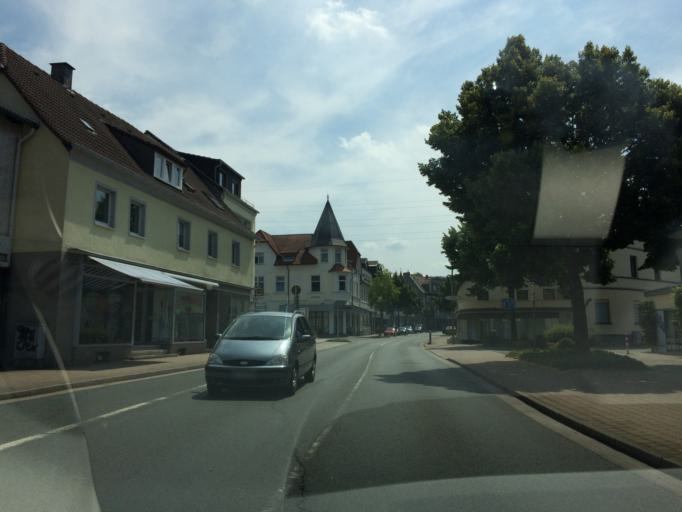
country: DE
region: North Rhine-Westphalia
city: Hemer
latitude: 51.3829
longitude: 7.7676
